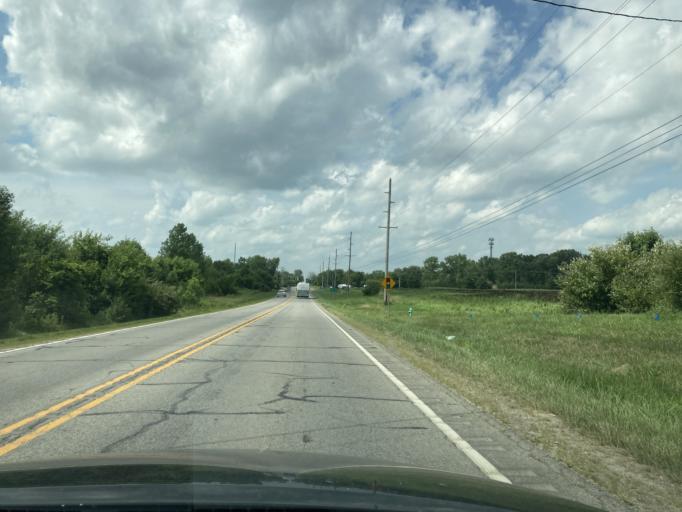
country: US
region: Indiana
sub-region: Boone County
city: Zionsville
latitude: 39.9952
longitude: -86.2630
